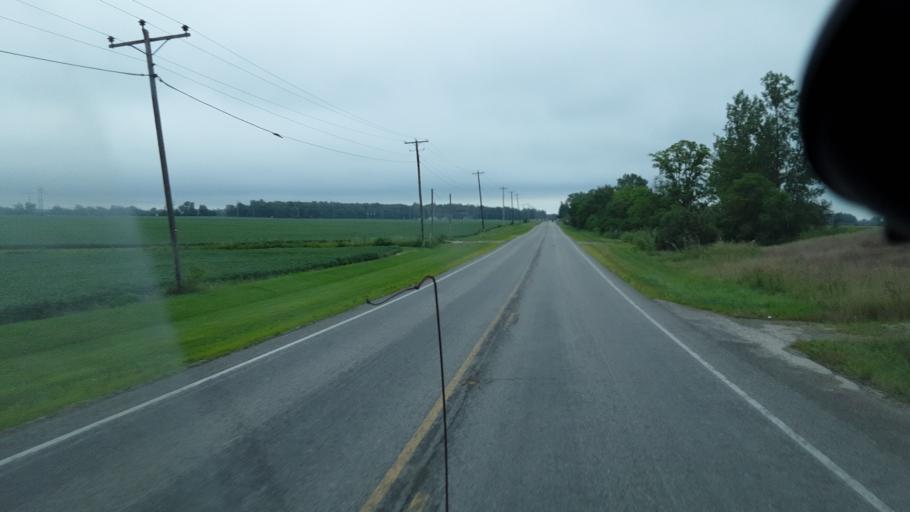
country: US
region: Indiana
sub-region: Adams County
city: Berne
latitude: 40.6606
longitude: -85.0517
